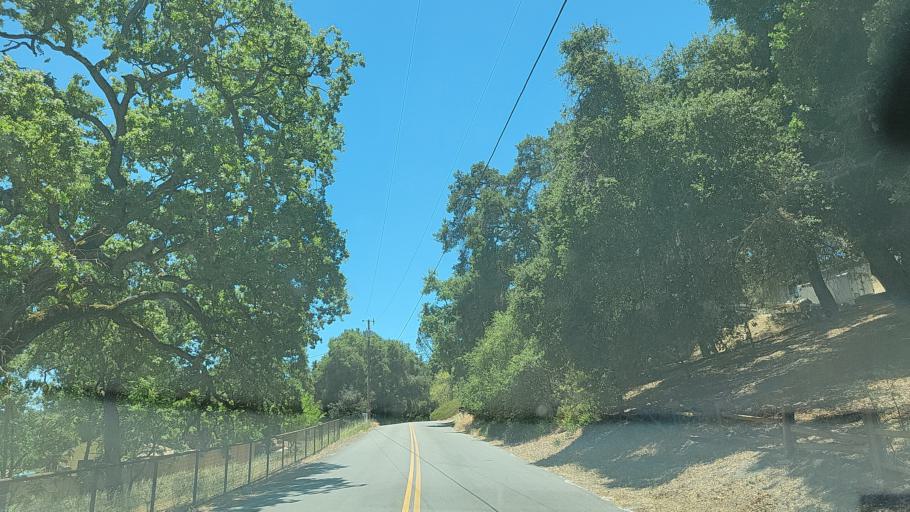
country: US
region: California
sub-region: San Luis Obispo County
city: Atascadero
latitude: 35.4981
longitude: -120.6706
